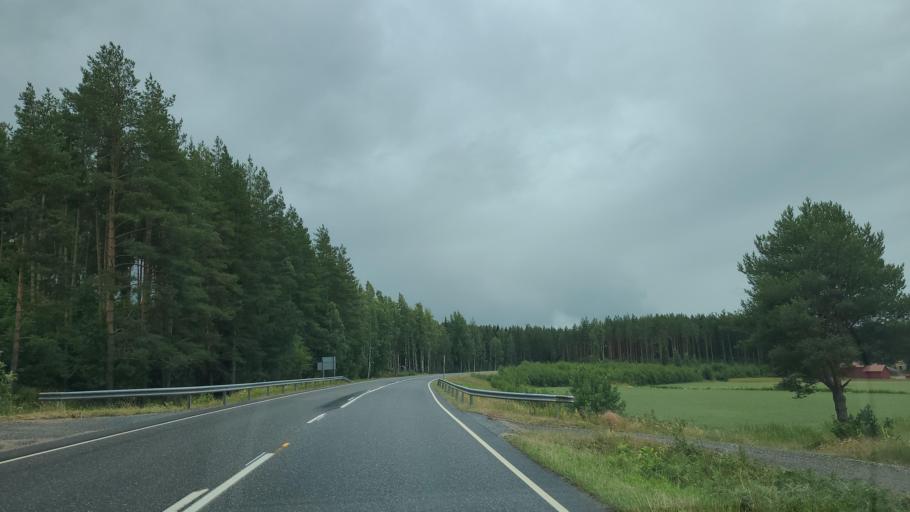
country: FI
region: Varsinais-Suomi
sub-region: Turku
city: Sauvo
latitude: 60.3284
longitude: 22.7140
